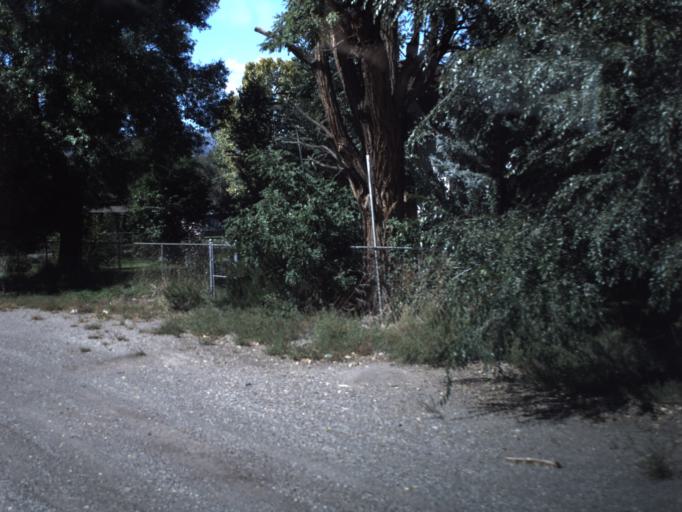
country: US
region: Utah
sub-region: Piute County
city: Junction
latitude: 38.2369
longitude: -112.2212
